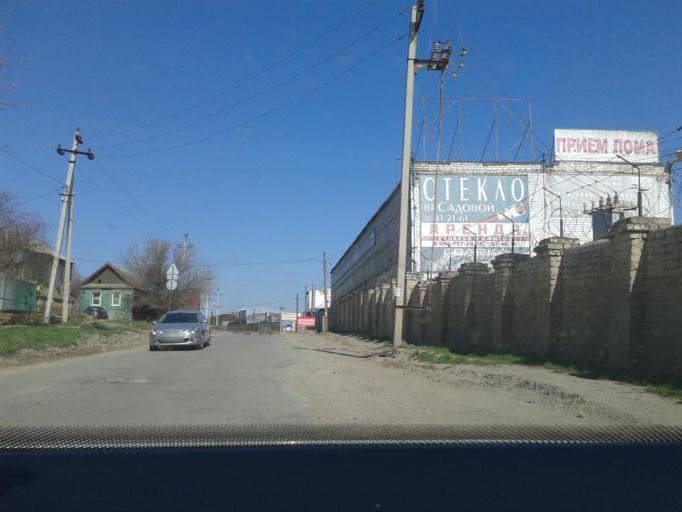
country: RU
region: Volgograd
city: Volgograd
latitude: 48.6799
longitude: 44.4624
